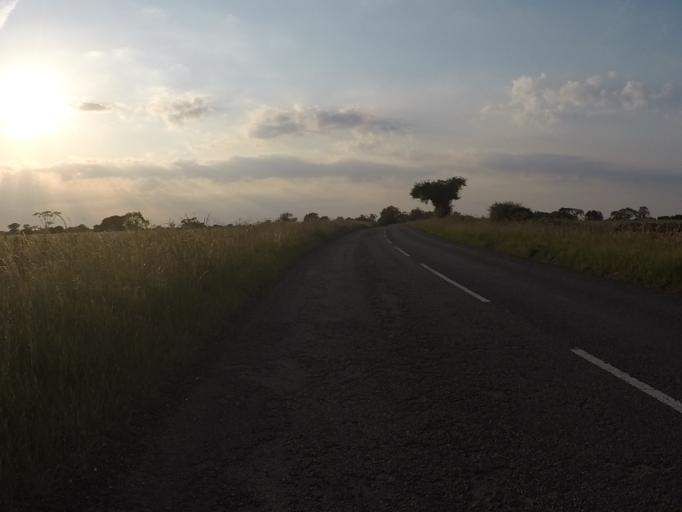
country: GB
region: England
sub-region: Oxfordshire
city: Charlbury
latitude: 51.9111
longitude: -1.4894
